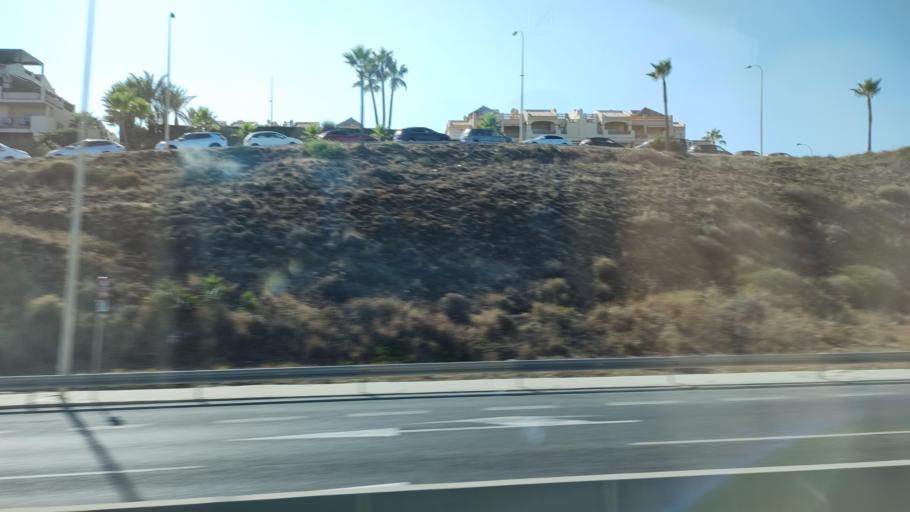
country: ES
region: Andalusia
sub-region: Provincia de Malaga
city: Fuengirola
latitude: 36.5121
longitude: -4.6352
